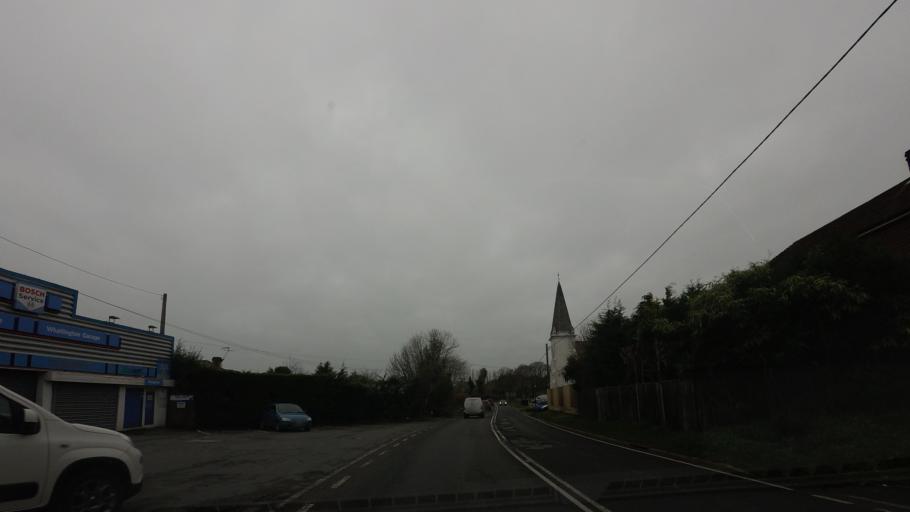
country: GB
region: England
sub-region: East Sussex
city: Battle
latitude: 50.9463
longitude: 0.5080
